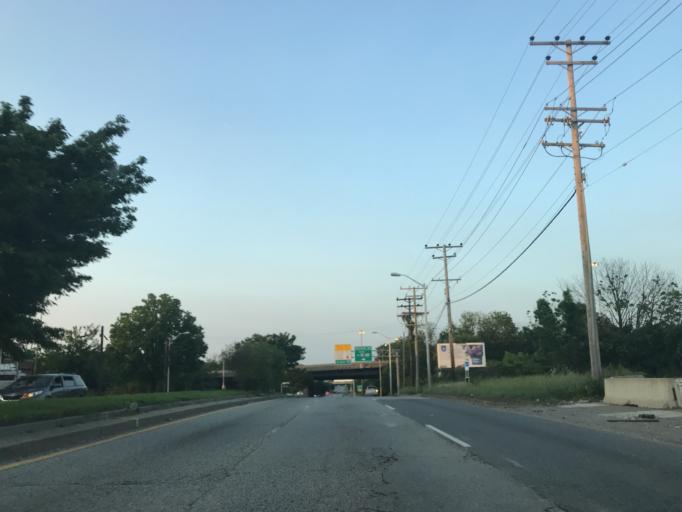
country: US
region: Maryland
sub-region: Baltimore County
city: Rosedale
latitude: 39.3053
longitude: -76.5367
